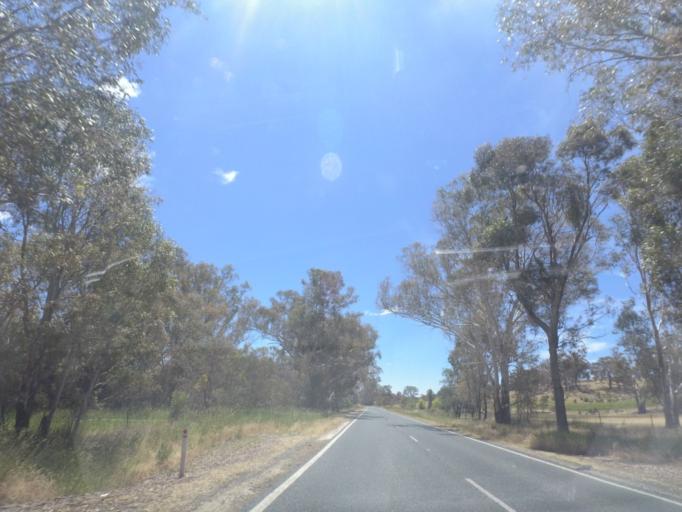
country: AU
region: Victoria
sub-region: Mount Alexander
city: Castlemaine
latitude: -37.1798
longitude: 144.1477
